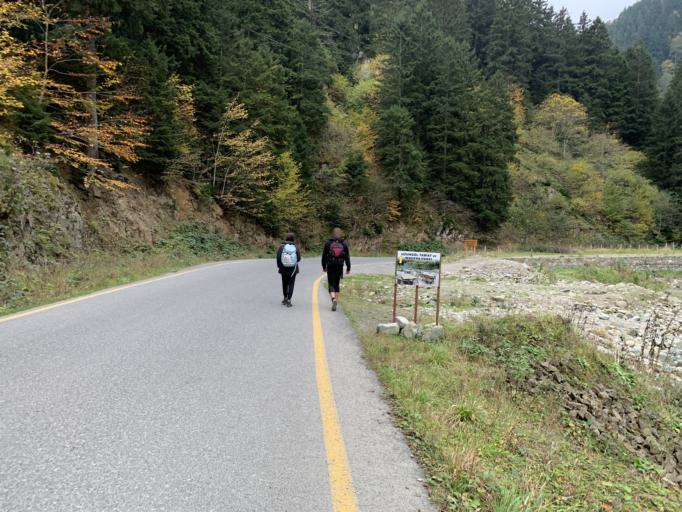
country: TR
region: Trabzon
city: Uzungol
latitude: 40.6027
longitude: 40.3175
